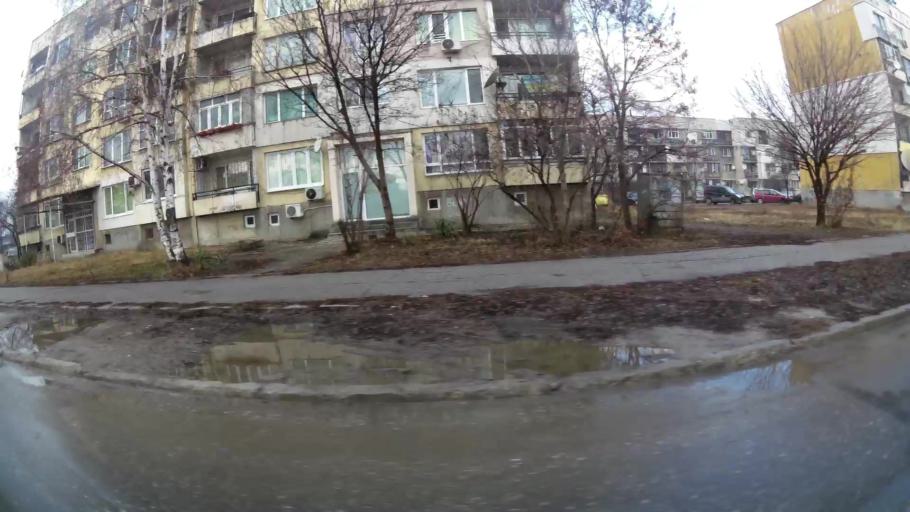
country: BG
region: Sofia-Capital
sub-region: Stolichna Obshtina
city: Sofia
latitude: 42.7404
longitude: 23.3445
